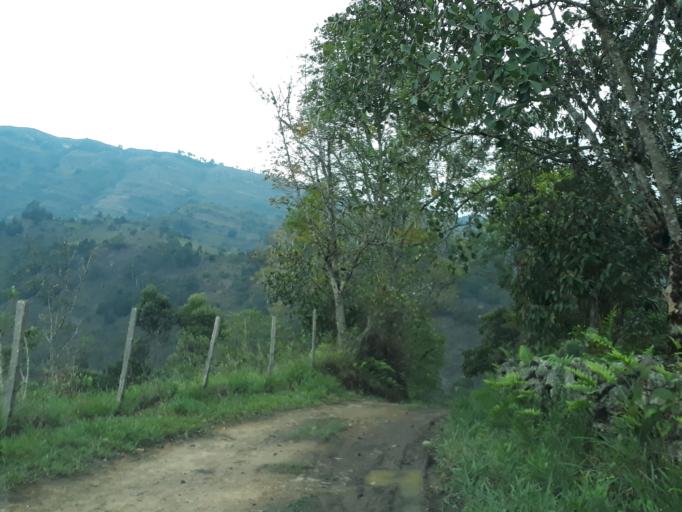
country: CO
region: Cundinamarca
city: Manta
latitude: 5.0596
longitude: -73.5225
